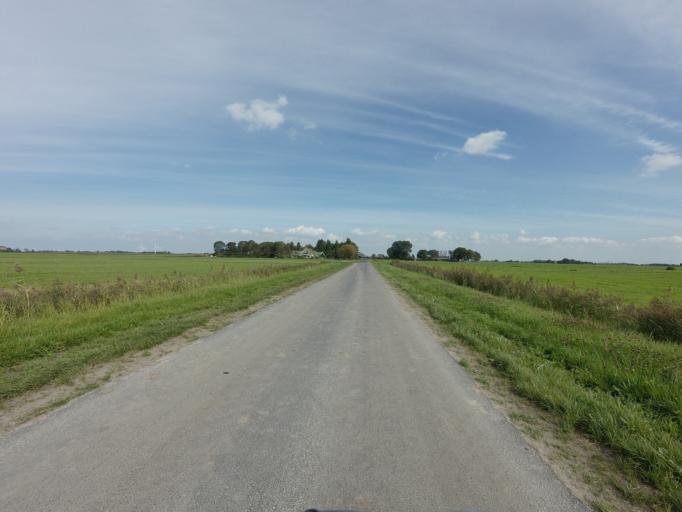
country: NL
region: Friesland
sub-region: Gemeente Harlingen
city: Harlingen
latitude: 53.1650
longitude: 5.4689
